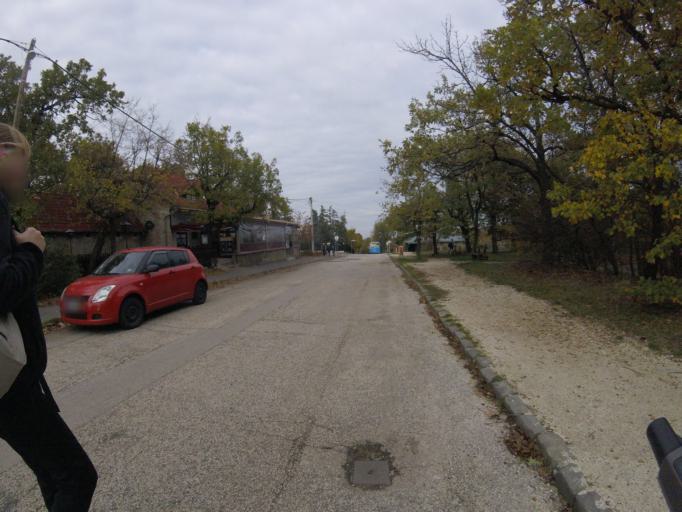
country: HU
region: Budapest
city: Budapest XII. keruelet
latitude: 47.4946
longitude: 18.9786
